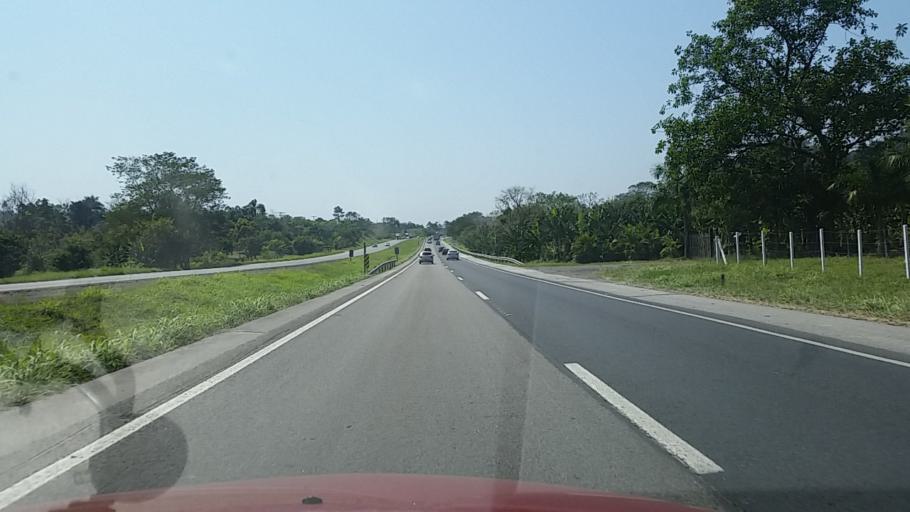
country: BR
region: Sao Paulo
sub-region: Miracatu
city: Miracatu
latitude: -24.2829
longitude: -47.4341
